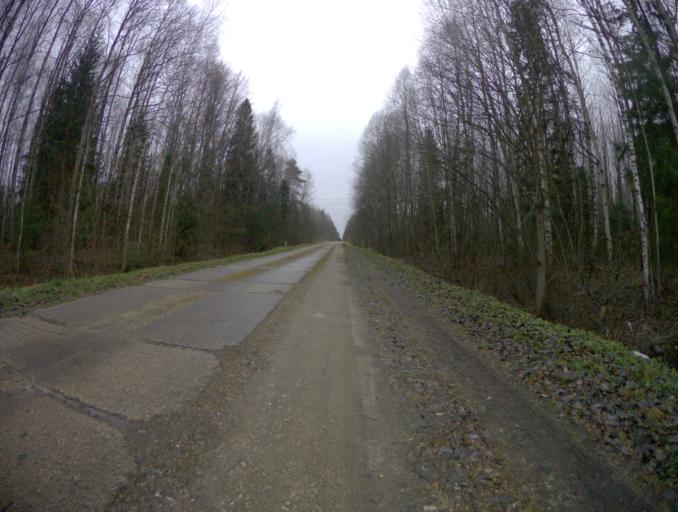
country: RU
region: Vladimir
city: Kommunar
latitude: 56.0386
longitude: 40.5237
